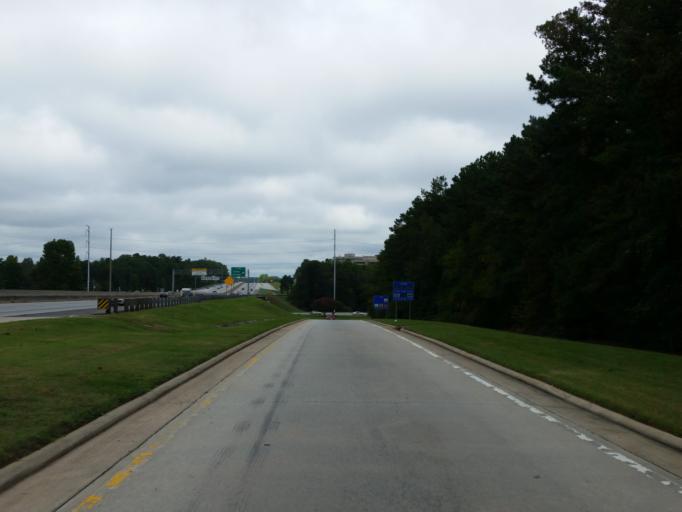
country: US
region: Georgia
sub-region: Fulton County
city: Sandy Springs
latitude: 33.9309
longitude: -84.3575
